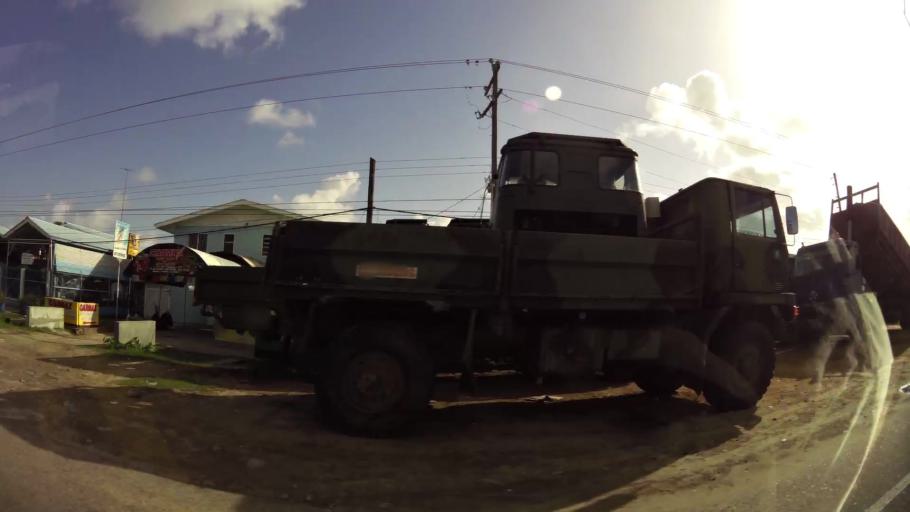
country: GY
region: Demerara-Mahaica
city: Georgetown
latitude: 6.8175
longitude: -58.0842
